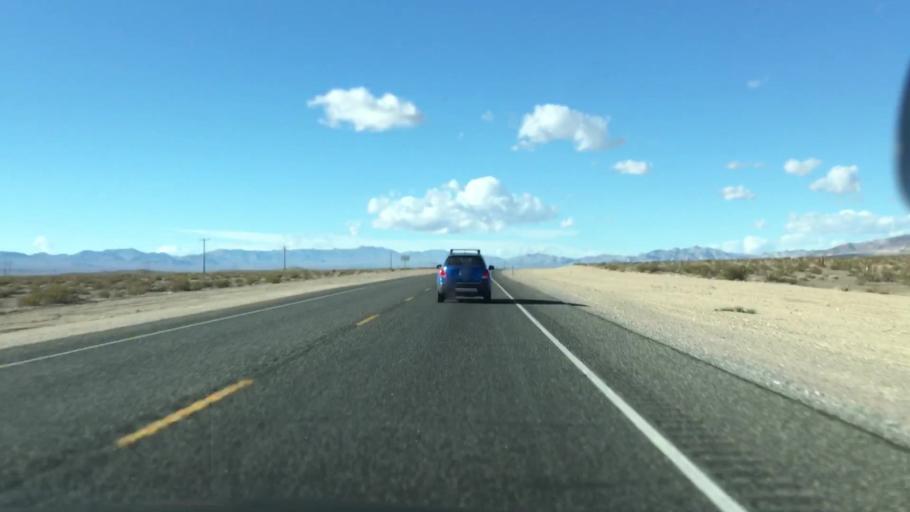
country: US
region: Nevada
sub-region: Nye County
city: Beatty
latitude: 36.7270
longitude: -116.6268
